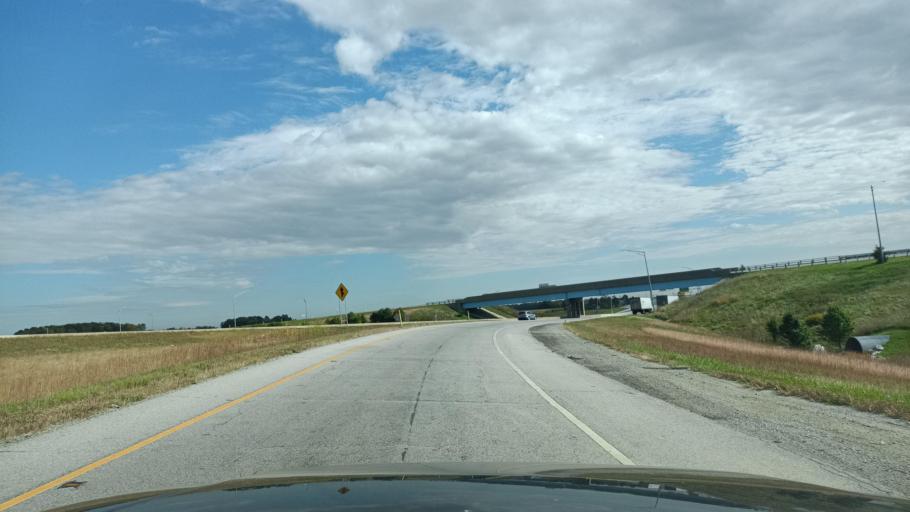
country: US
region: Indiana
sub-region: Huntington County
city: Roanoke
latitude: 40.9600
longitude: -85.2906
